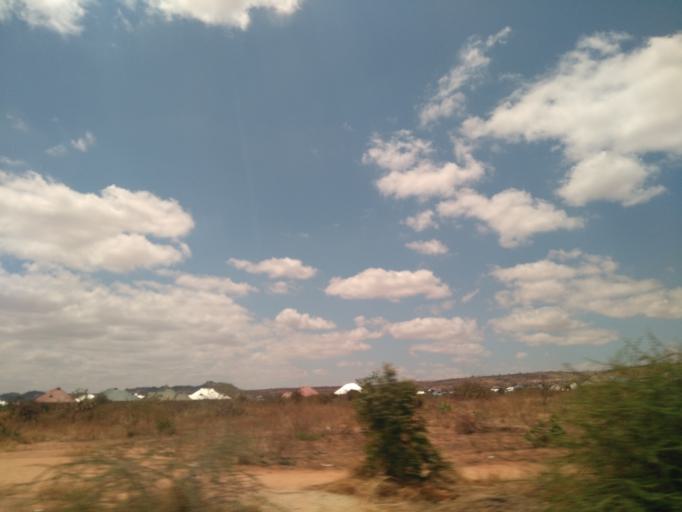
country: TZ
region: Dodoma
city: Kisasa
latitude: -6.1772
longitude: 35.7905
